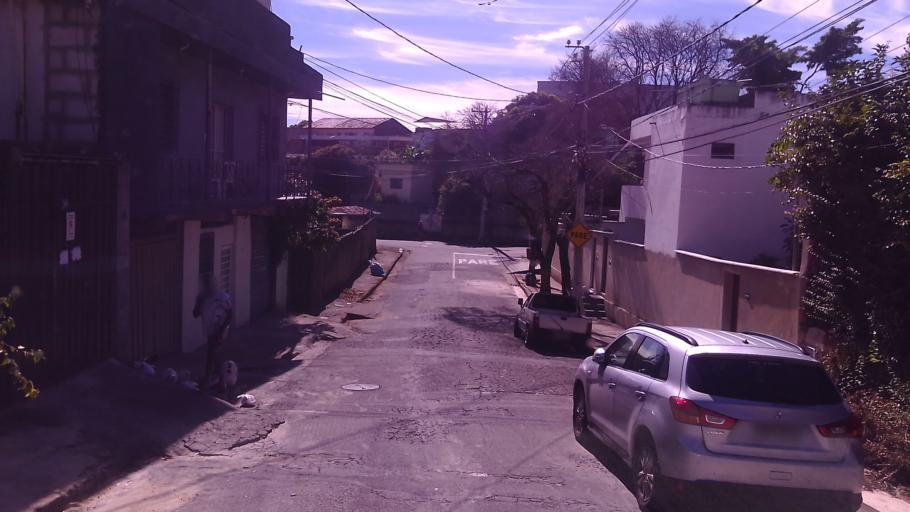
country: BR
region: Minas Gerais
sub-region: Contagem
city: Contagem
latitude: -19.9042
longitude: -44.0117
